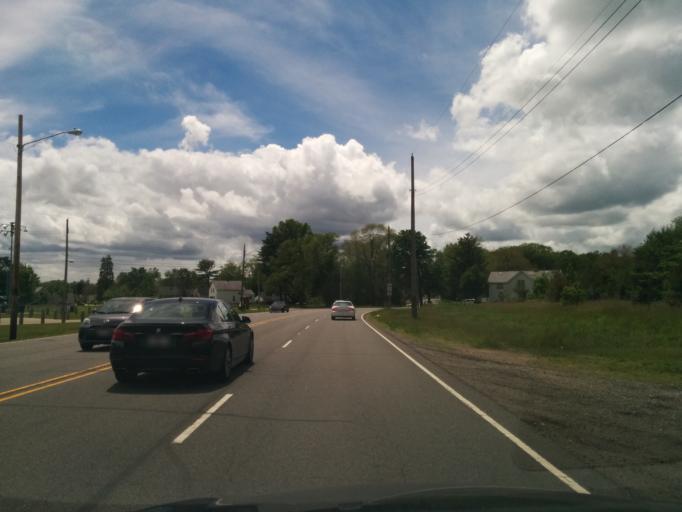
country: US
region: Indiana
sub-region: LaPorte County
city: Michigan City
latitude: 41.7157
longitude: -86.9113
